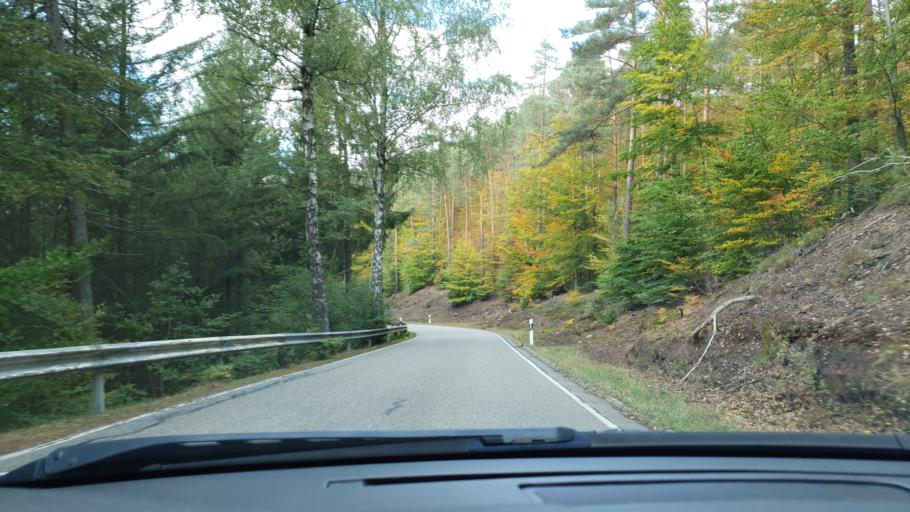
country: DE
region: Rheinland-Pfalz
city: Waldleiningen
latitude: 49.4056
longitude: 7.8345
